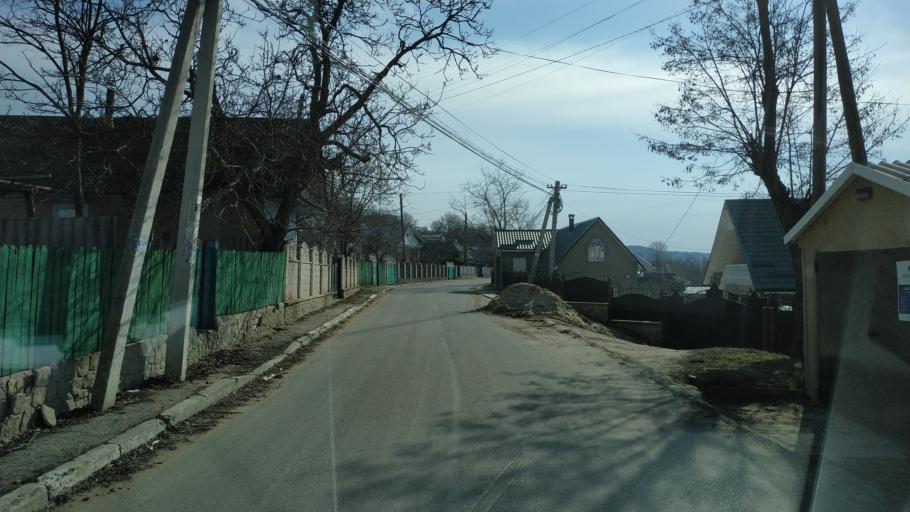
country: MD
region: Nisporeni
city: Nisporeni
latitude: 47.1745
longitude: 28.1277
